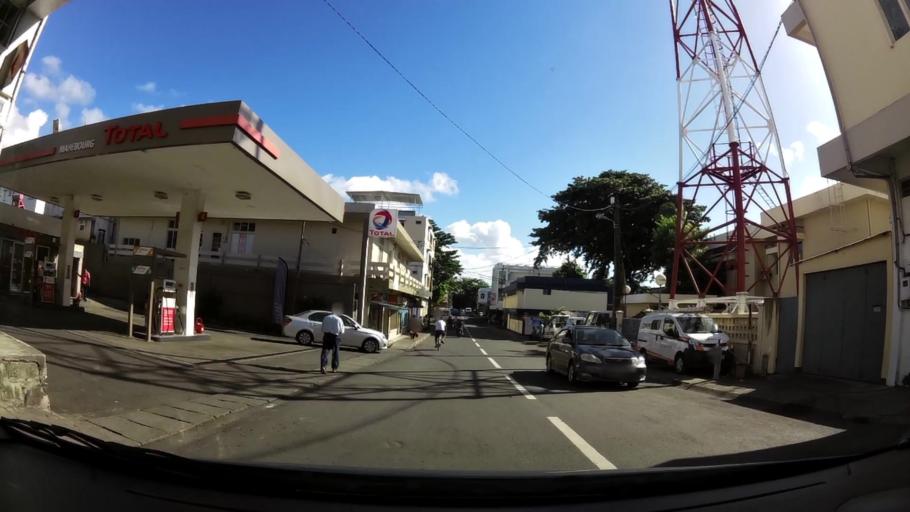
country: MU
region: Grand Port
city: Mahebourg
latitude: -20.4080
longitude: 57.7059
